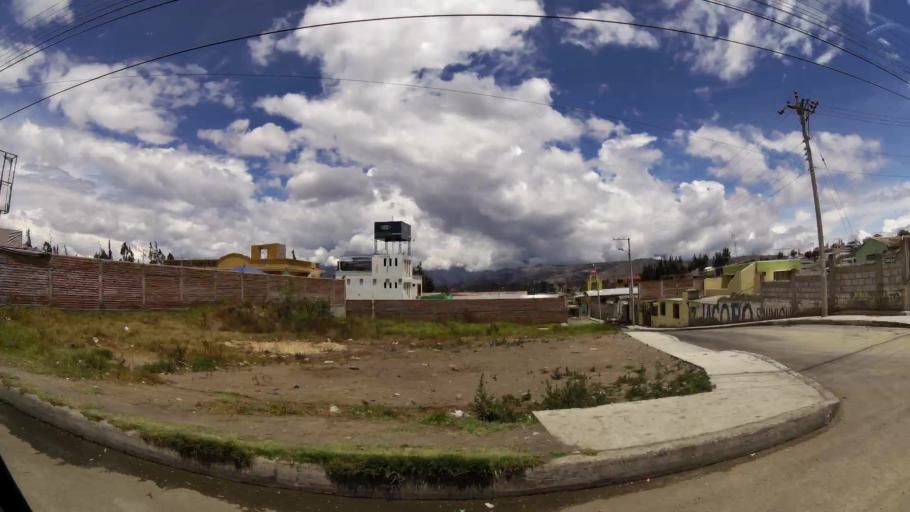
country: EC
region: Tungurahua
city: Ambato
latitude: -1.2876
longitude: -78.6067
